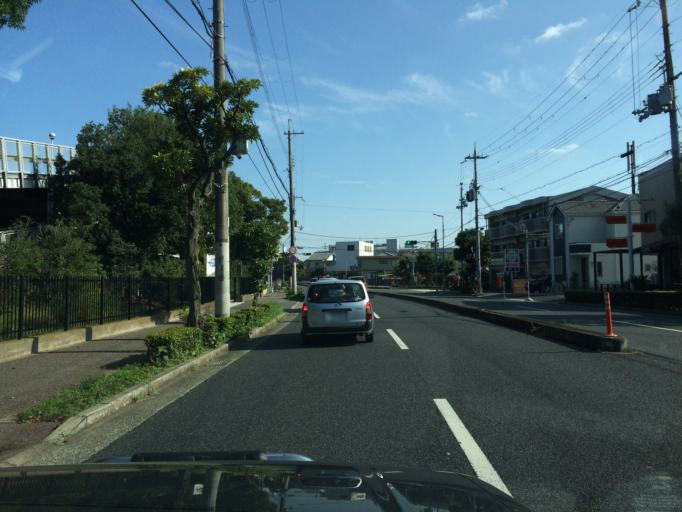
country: JP
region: Hyogo
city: Itami
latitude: 34.7884
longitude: 135.3911
